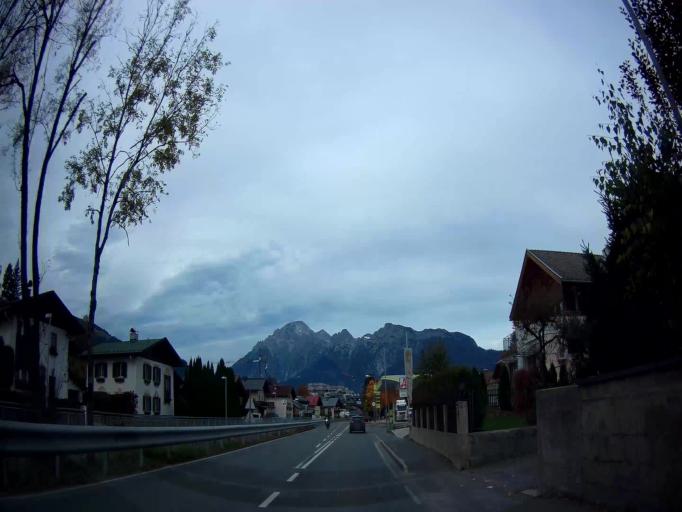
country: AT
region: Salzburg
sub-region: Politischer Bezirk Zell am See
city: Saalfelden am Steinernen Meer
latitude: 47.4226
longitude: 12.8506
